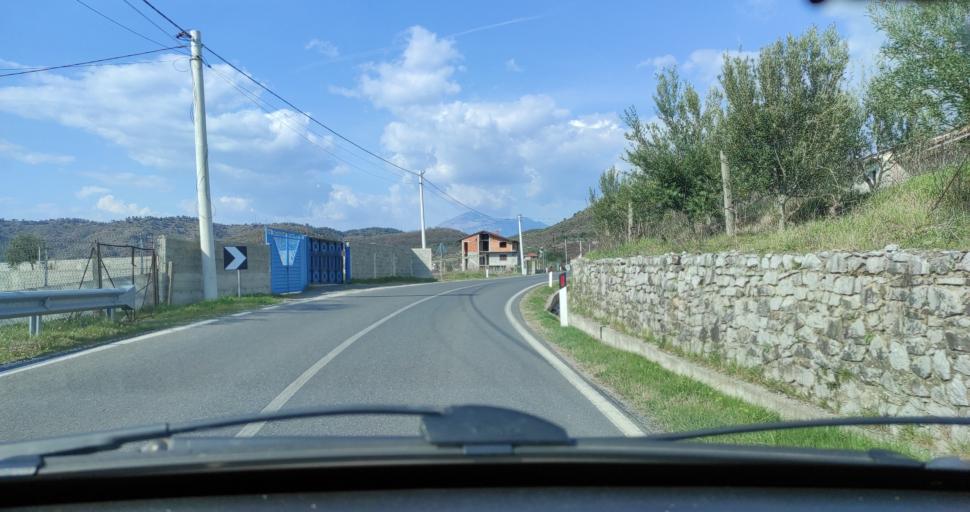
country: AL
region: Shkoder
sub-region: Rrethi i Shkodres
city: Guri i Zi
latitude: 42.0507
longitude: 19.5595
